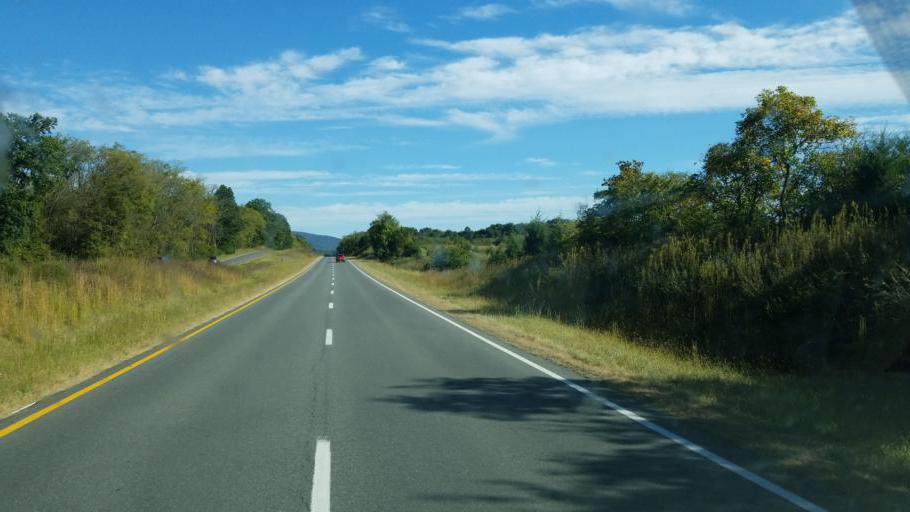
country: US
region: Virginia
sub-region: Warren County
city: Shenandoah Farms
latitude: 39.0668
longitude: -78.0568
